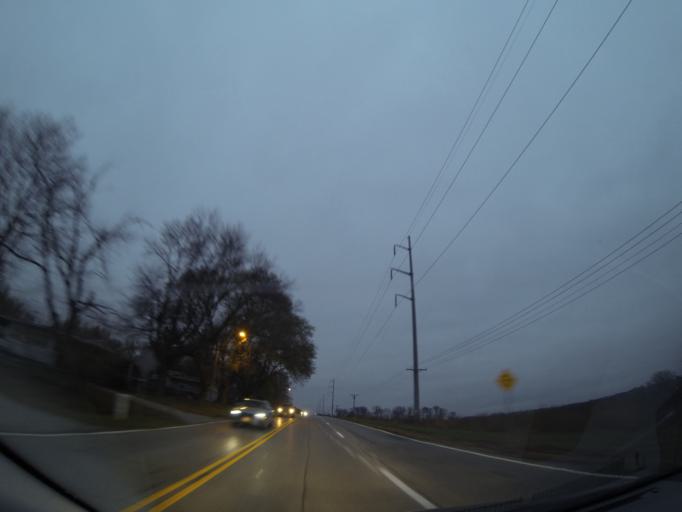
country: US
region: Nebraska
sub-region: Douglas County
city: Elkhorn
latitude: 41.2678
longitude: -96.1772
